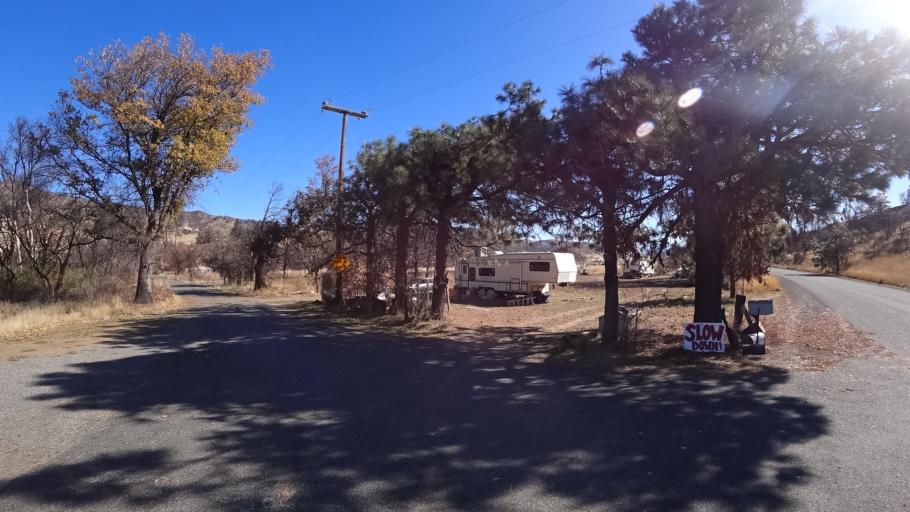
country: US
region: California
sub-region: Siskiyou County
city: Yreka
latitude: 41.9319
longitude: -122.5886
